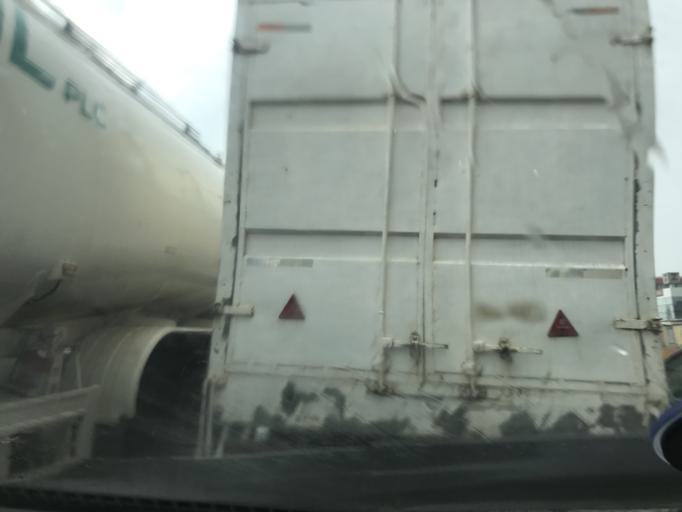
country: NG
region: Lagos
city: Oshodi
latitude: 6.5536
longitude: 3.3473
